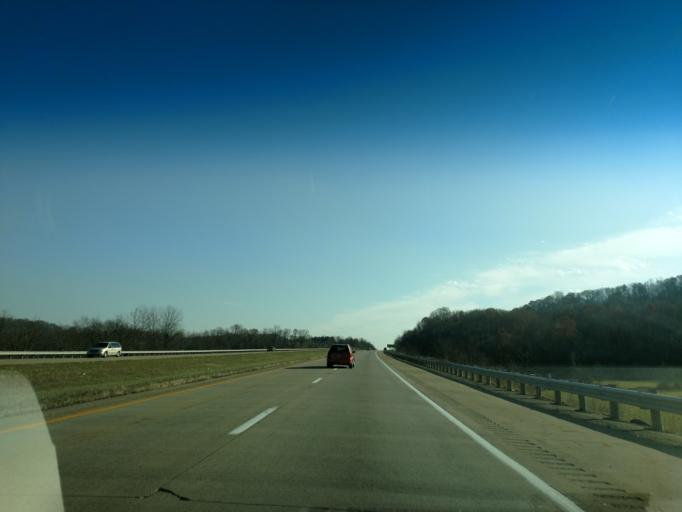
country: US
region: Ohio
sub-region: Noble County
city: Caldwell
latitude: 39.7295
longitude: -81.5241
